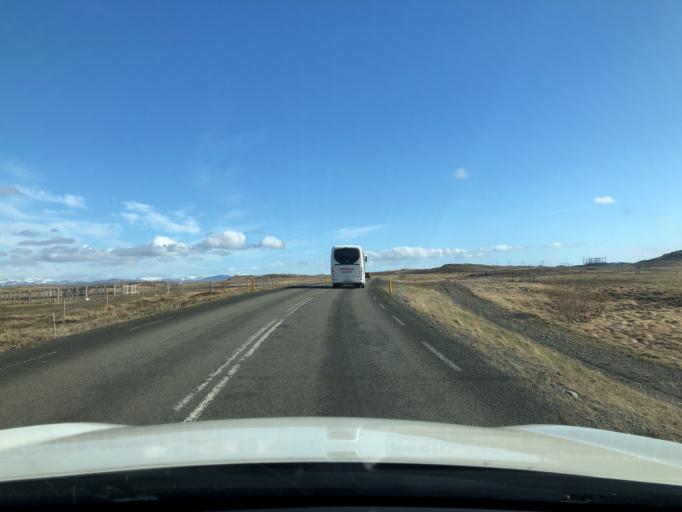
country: IS
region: West
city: Borgarnes
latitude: 64.5482
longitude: -21.7335
